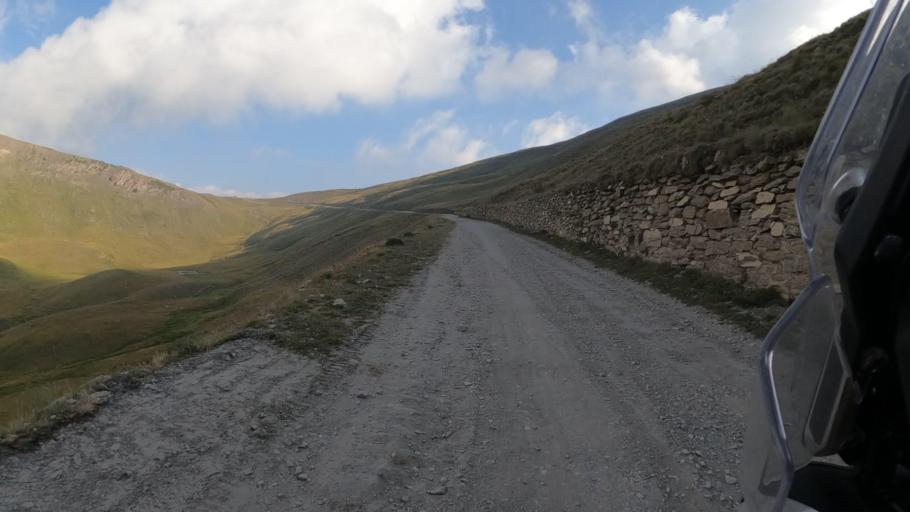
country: IT
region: Piedmont
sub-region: Provincia di Torino
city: Exilles
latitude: 45.0664
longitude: 6.9632
